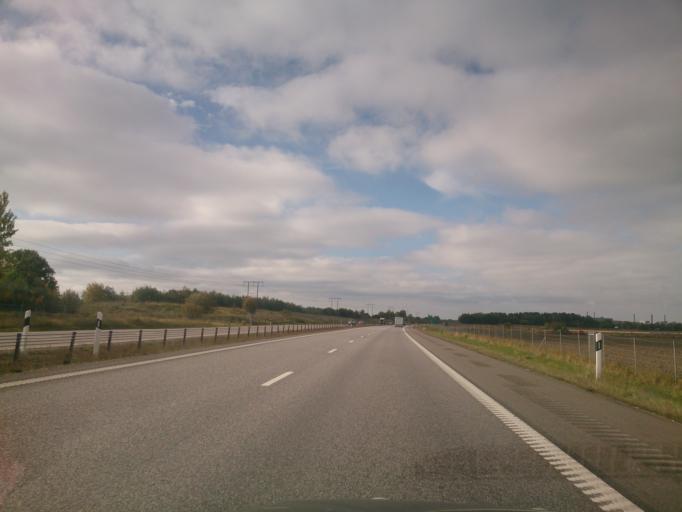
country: SE
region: OEstergoetland
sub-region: Linkopings Kommun
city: Ekangen
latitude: 58.4376
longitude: 15.7009
